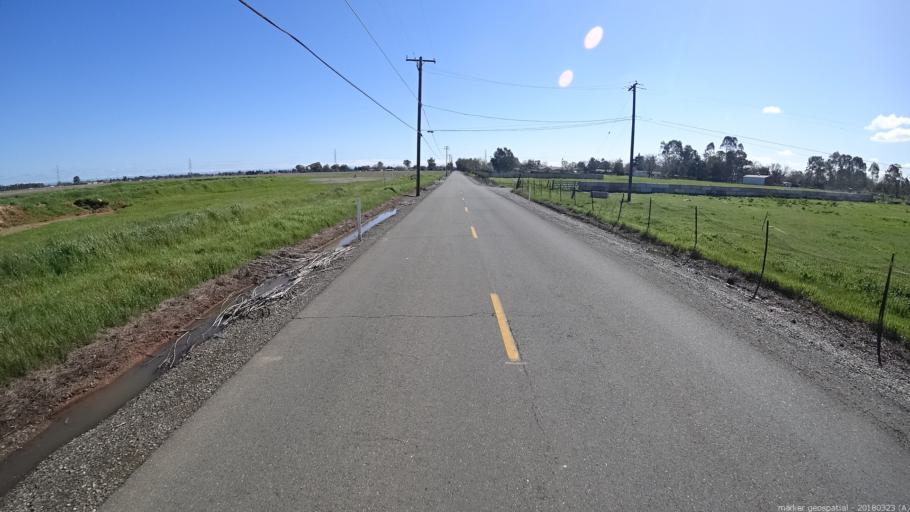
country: US
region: California
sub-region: Sacramento County
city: Rio Linda
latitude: 38.7048
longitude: -121.4366
